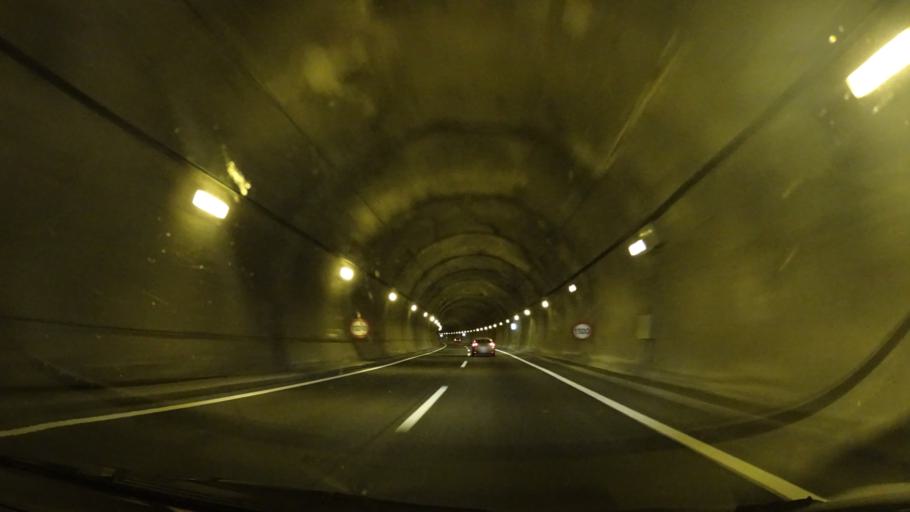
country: ES
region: Castille and Leon
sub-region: Provincia de Leon
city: Soto y Amio
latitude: 42.8488
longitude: -5.8739
